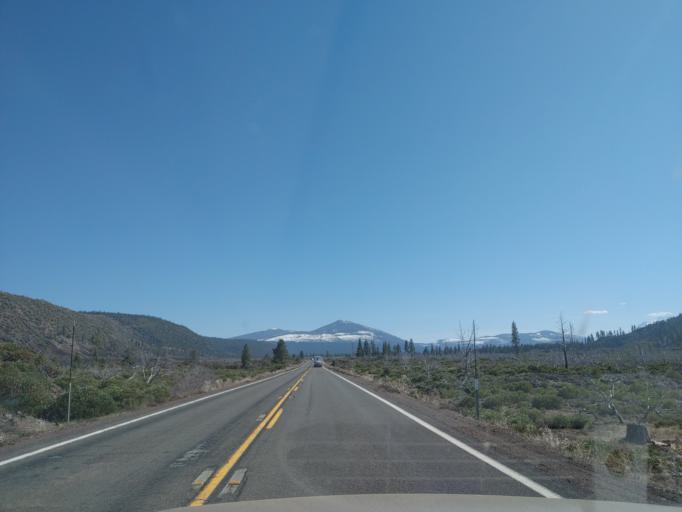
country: US
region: California
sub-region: Shasta County
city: Burney
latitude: 40.7101
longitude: -121.4207
